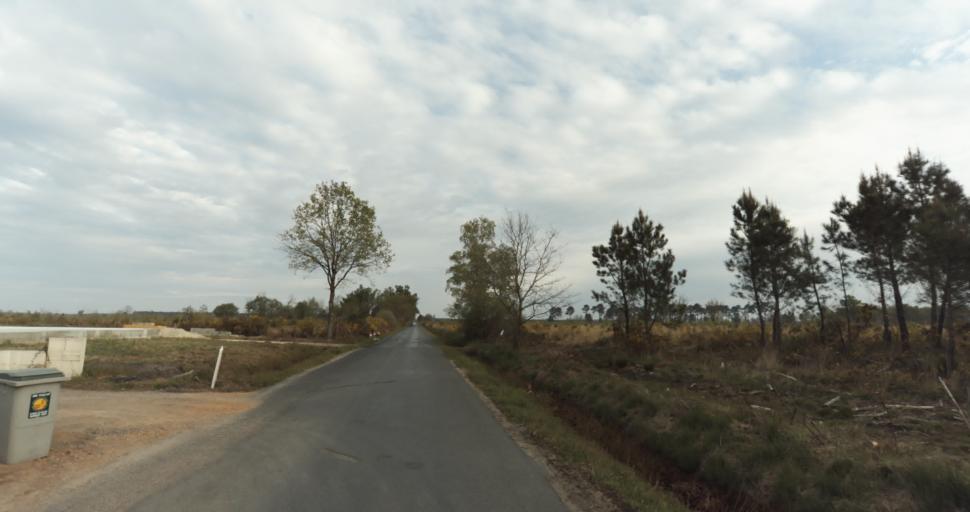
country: FR
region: Aquitaine
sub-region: Departement de la Gironde
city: Saint-Aubin-de-Medoc
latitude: 44.7774
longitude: -0.7424
